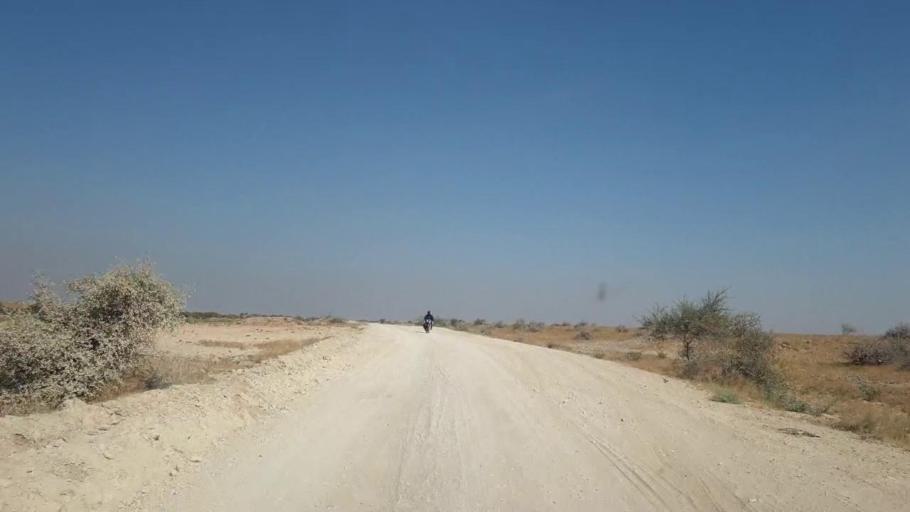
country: PK
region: Sindh
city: Thatta
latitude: 25.2271
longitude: 67.8026
